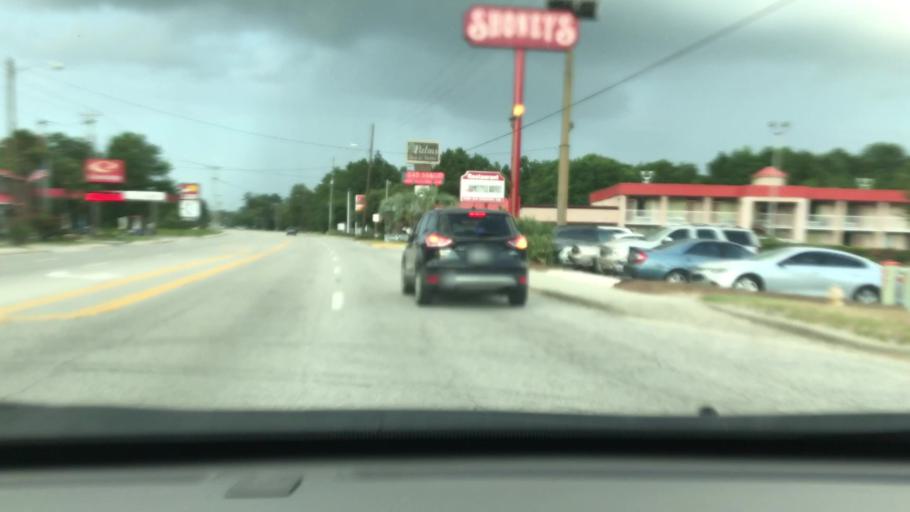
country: US
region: South Carolina
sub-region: Colleton County
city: Walterboro
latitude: 32.8801
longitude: -80.7097
